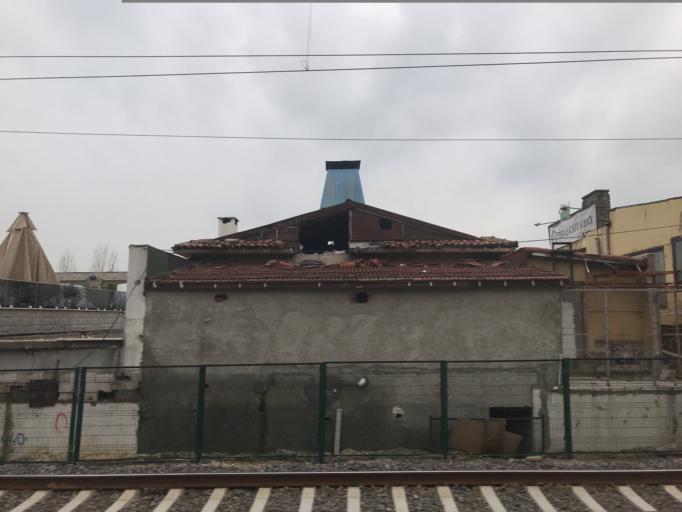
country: TR
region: Istanbul
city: Maltepe
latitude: 40.9398
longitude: 29.1126
